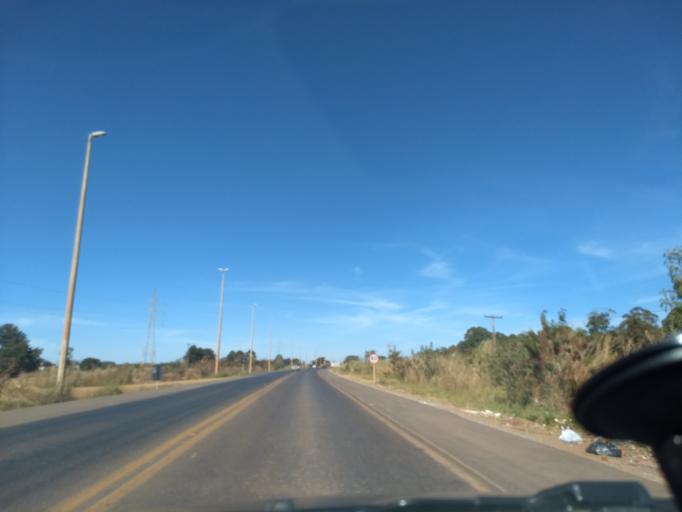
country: BR
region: Federal District
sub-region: Brasilia
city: Brasilia
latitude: -15.7735
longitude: -48.0458
